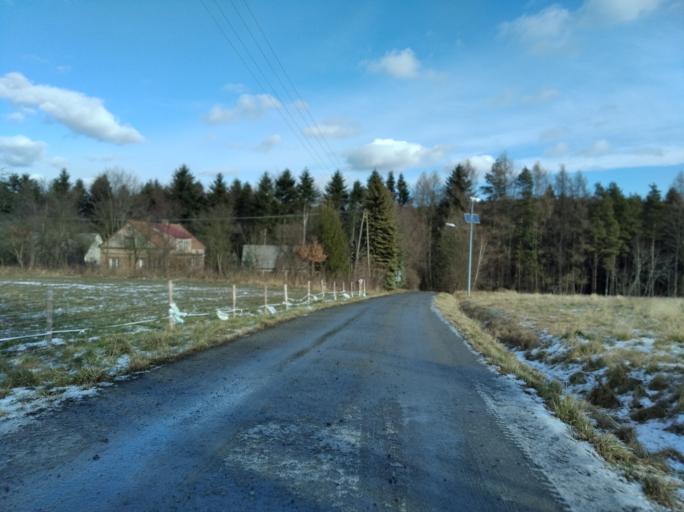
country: PL
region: Subcarpathian Voivodeship
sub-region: Powiat strzyzowski
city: Strzyzow
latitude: 49.9024
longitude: 21.7672
